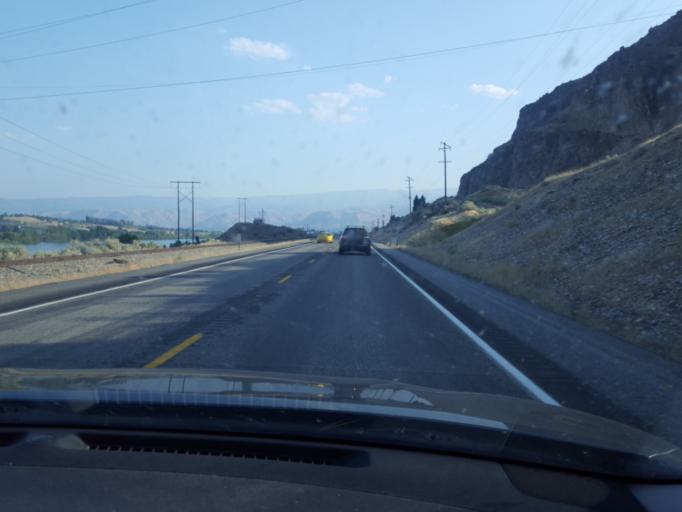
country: US
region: Washington
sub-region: Chelan County
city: Sunnyslope
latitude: 47.5016
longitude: -120.3110
